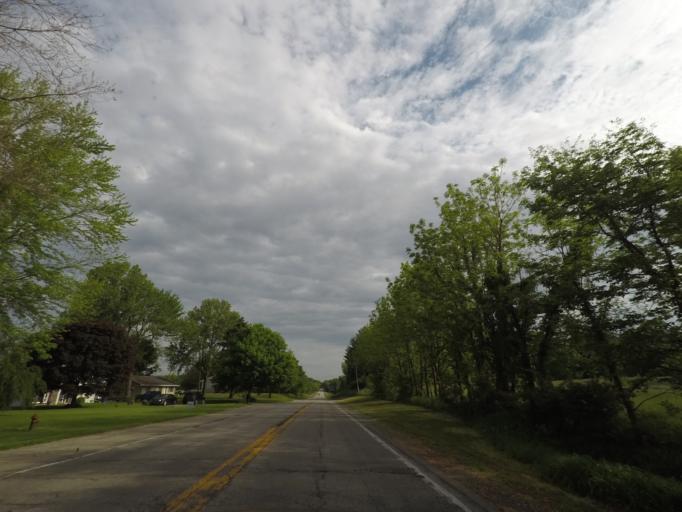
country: US
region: Illinois
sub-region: Logan County
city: Mount Pulaski
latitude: 40.0471
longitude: -89.2820
